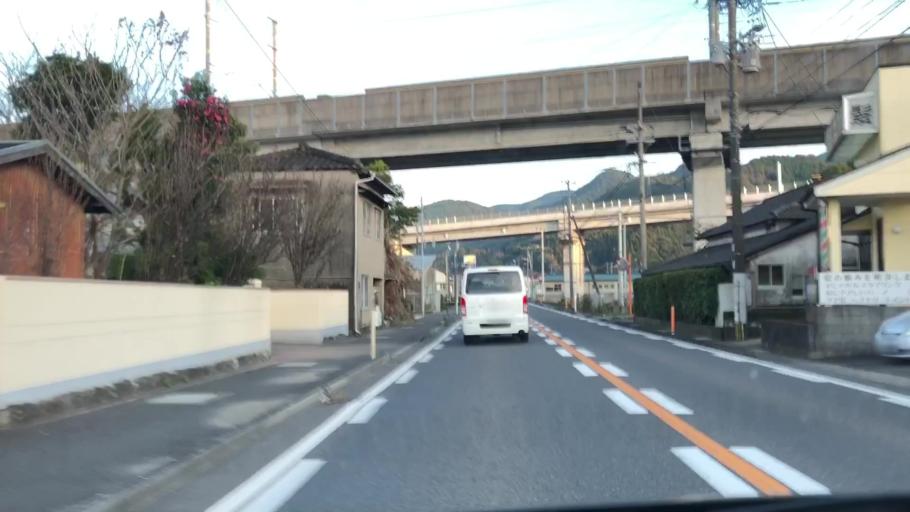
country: JP
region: Kumamoto
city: Minamata
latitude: 32.2331
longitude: 130.4512
